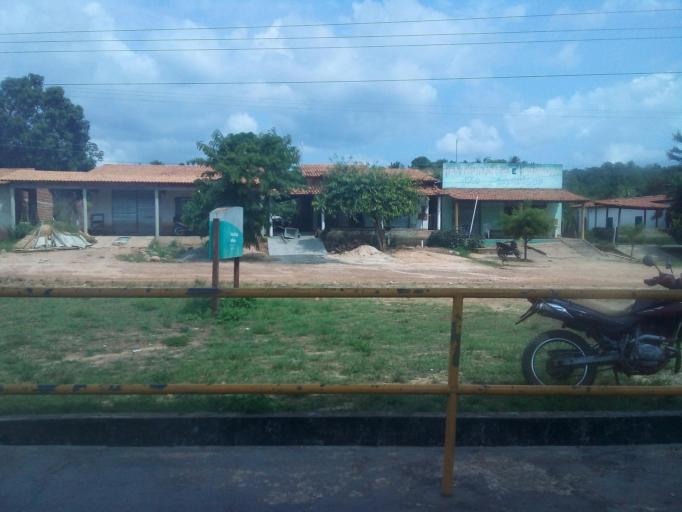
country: BR
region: Maranhao
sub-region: Santa Ines
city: Santa Ines
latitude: -3.8785
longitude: -46.1995
